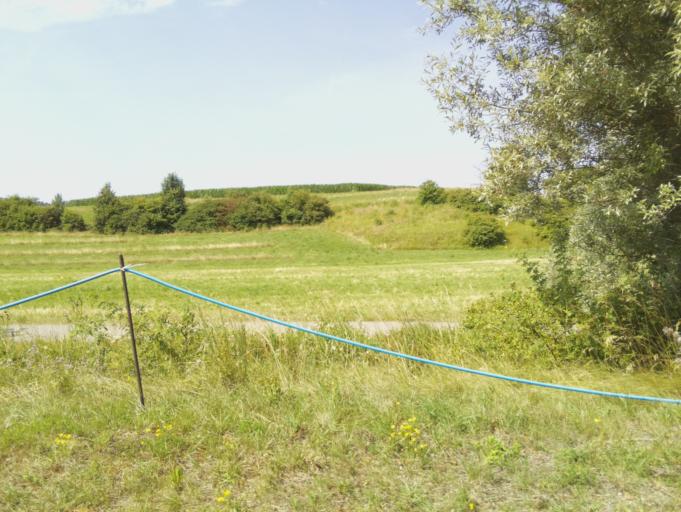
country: CH
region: Zurich
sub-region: Bezirk Andelfingen
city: Henggart
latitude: 47.5769
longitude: 8.6766
